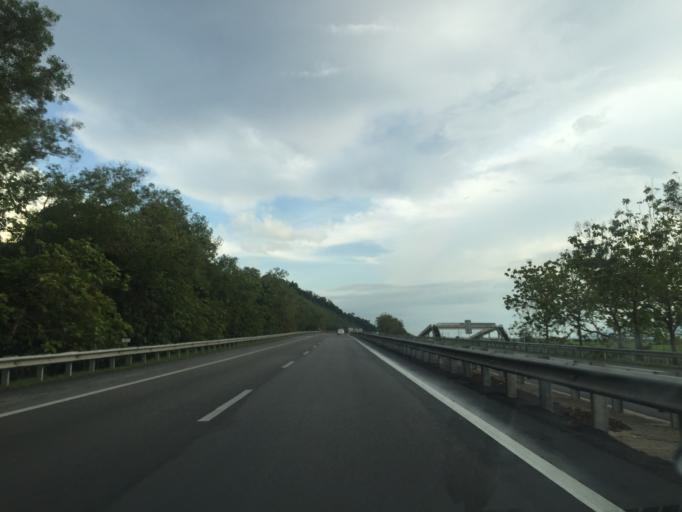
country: MY
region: Kedah
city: Gurun
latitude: 5.9450
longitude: 100.4566
